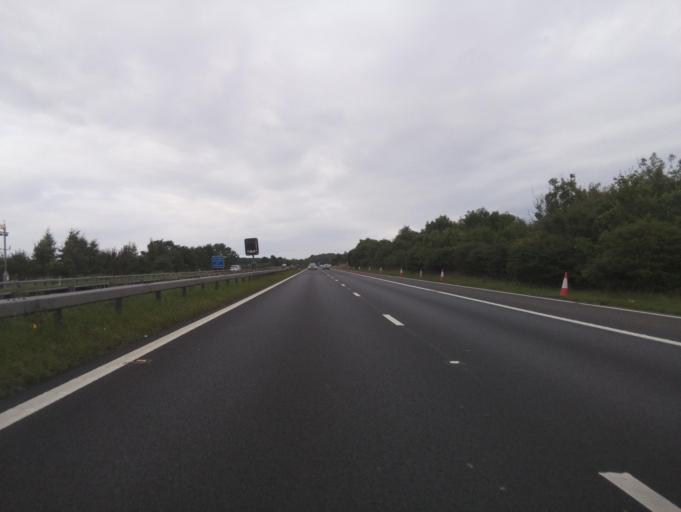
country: GB
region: England
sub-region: County Durham
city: Bishop Middleham
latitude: 54.6742
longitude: -1.5002
